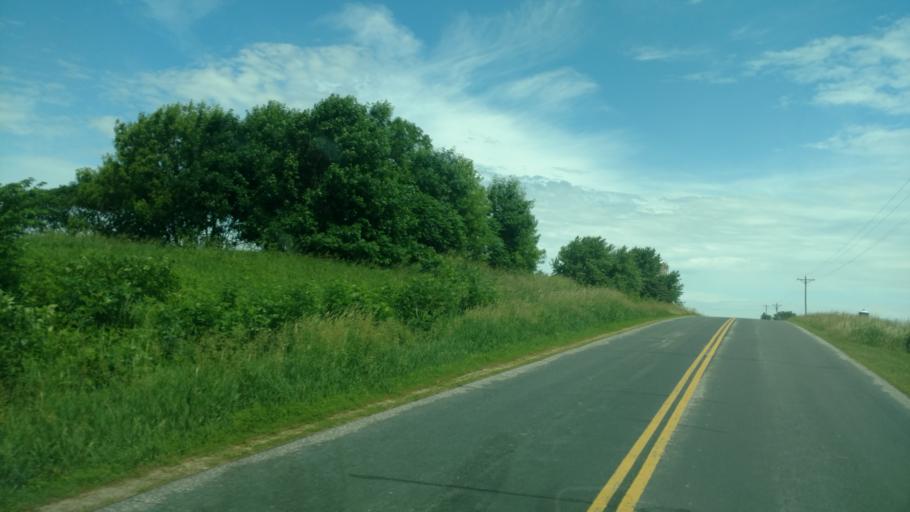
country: US
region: Wisconsin
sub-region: Vernon County
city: Hillsboro
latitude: 43.7474
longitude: -90.4329
